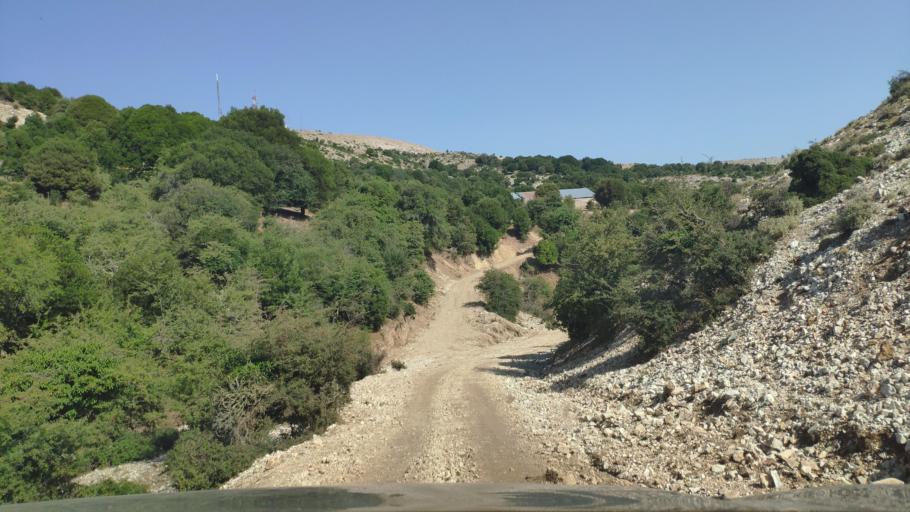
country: GR
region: West Greece
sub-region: Nomos Aitolias kai Akarnanias
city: Monastirakion
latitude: 38.8008
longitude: 20.9968
